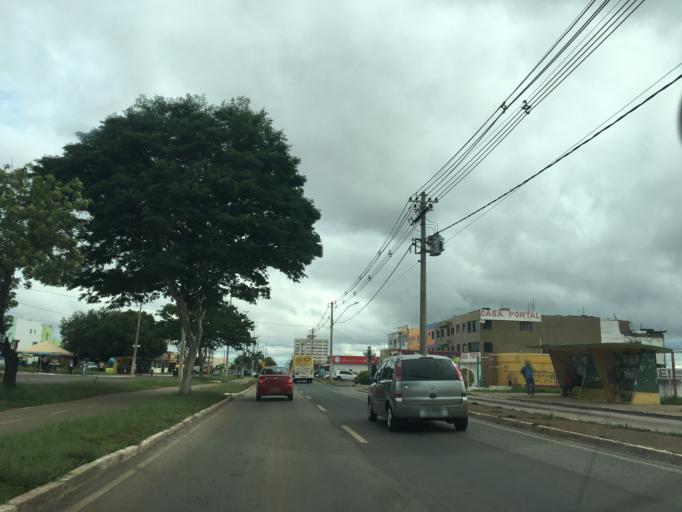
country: BR
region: Goias
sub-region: Luziania
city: Luziania
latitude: -16.0389
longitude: -48.0342
